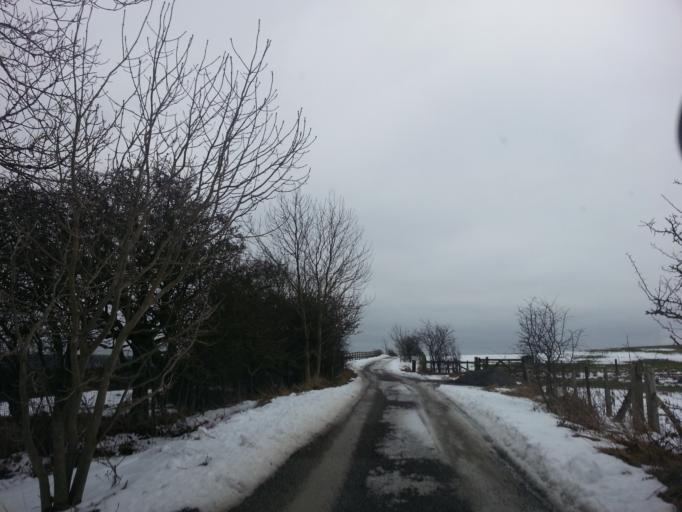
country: GB
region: England
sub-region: County Durham
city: Tow Law
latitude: 54.7725
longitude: -1.7932
